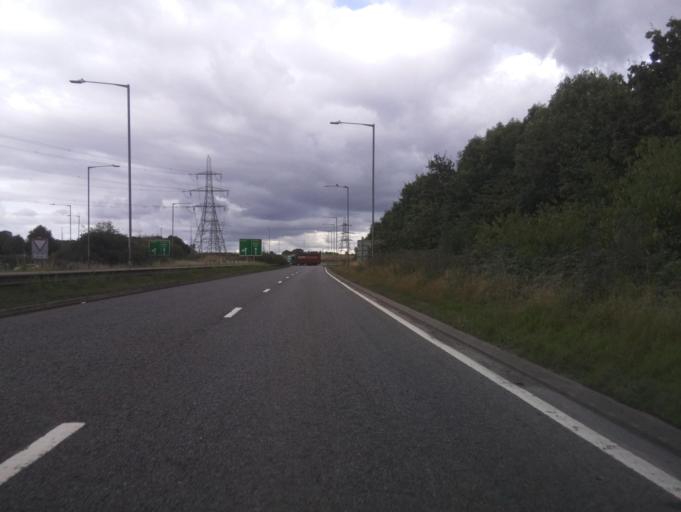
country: GB
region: England
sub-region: Warwickshire
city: Curdworth
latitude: 52.5278
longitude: -1.7235
